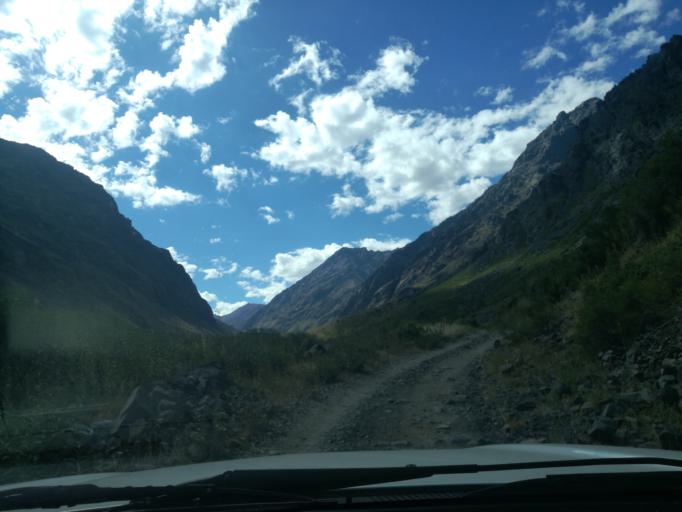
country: CL
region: O'Higgins
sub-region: Provincia de Cachapoal
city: Machali
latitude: -34.3926
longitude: -70.2753
